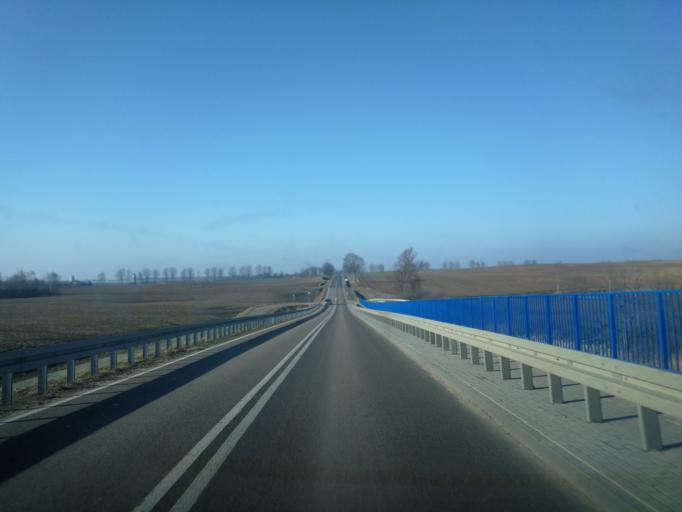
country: PL
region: Warmian-Masurian Voivodeship
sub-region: Powiat ilawski
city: Lubawa
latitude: 53.4113
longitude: 19.7938
